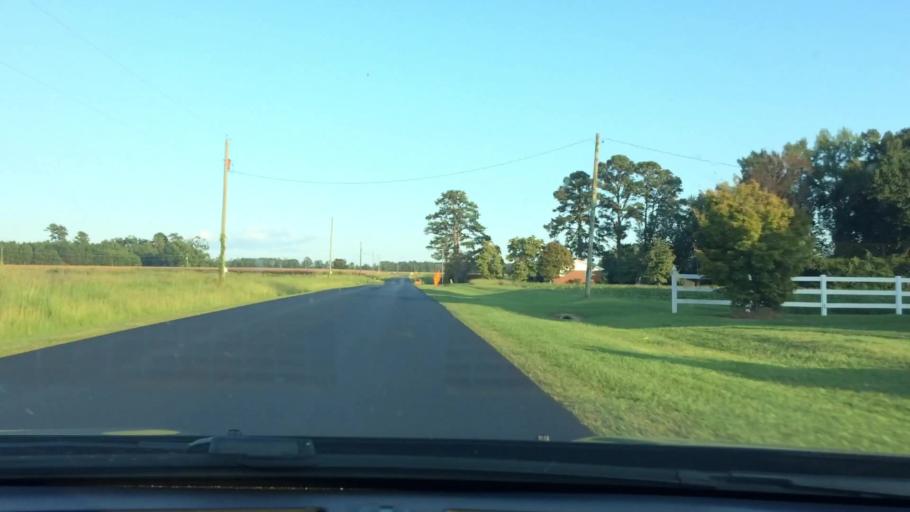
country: US
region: North Carolina
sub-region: Pitt County
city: Ayden
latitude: 35.4458
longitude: -77.4585
